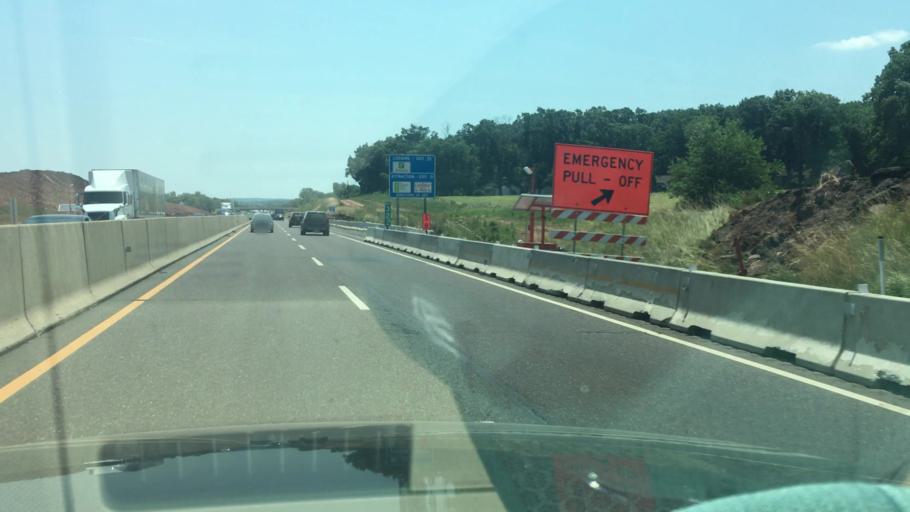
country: US
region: Pennsylvania
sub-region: Montgomery County
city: Harleysville
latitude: 40.2775
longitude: -75.3598
